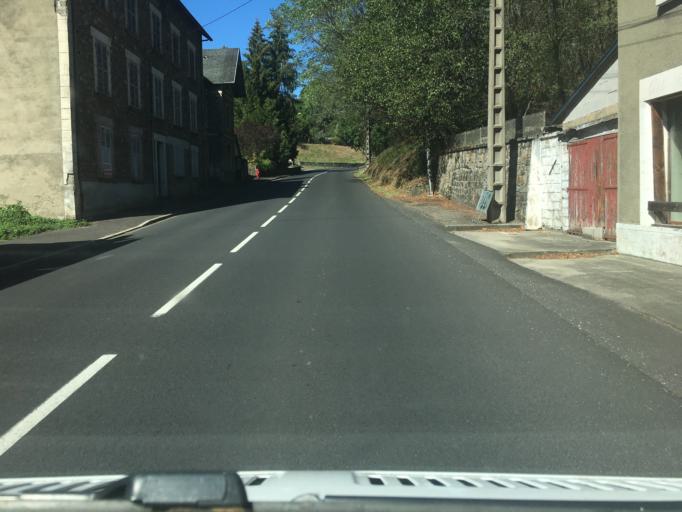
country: FR
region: Limousin
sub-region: Departement de la Correze
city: Bort-les-Orgues
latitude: 45.4112
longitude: 2.5035
